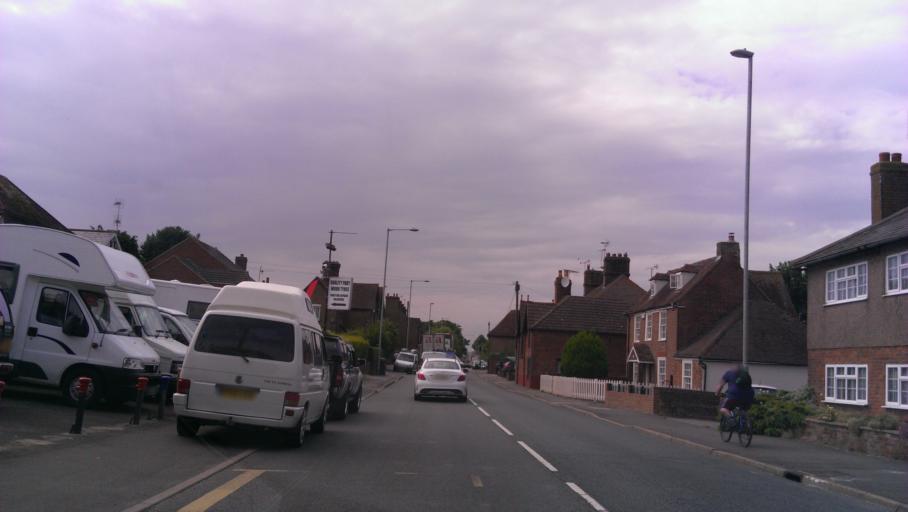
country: GB
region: England
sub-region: Kent
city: Teynham
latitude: 51.3342
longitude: 0.7696
